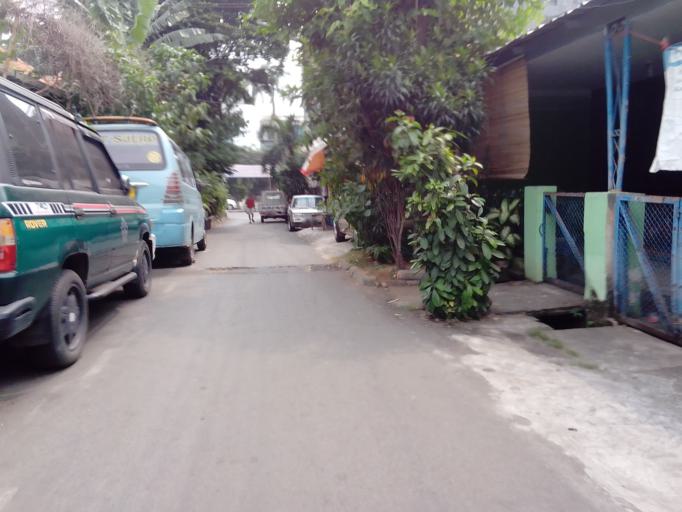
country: ID
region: Jakarta Raya
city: Jakarta
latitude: -6.1906
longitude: 106.8070
